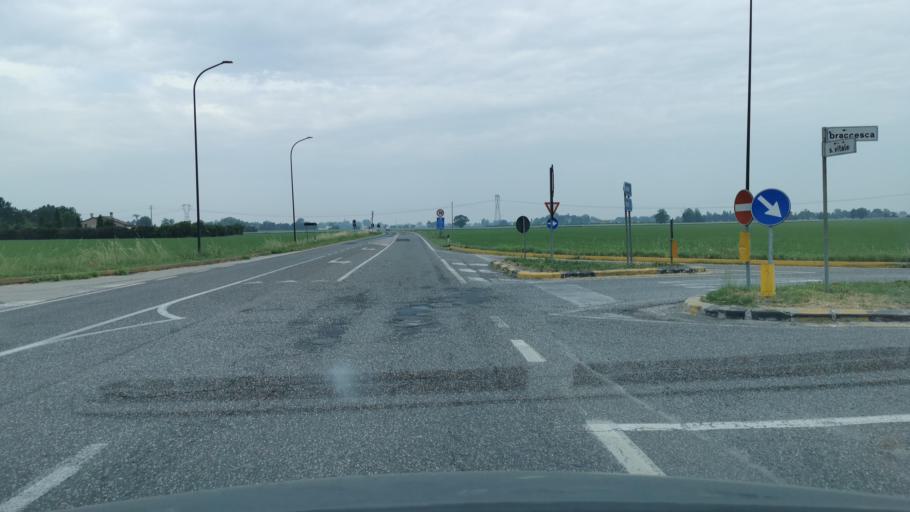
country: IT
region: Emilia-Romagna
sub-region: Provincia di Ravenna
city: Fornace Zarattini
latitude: 44.4065
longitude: 12.1105
